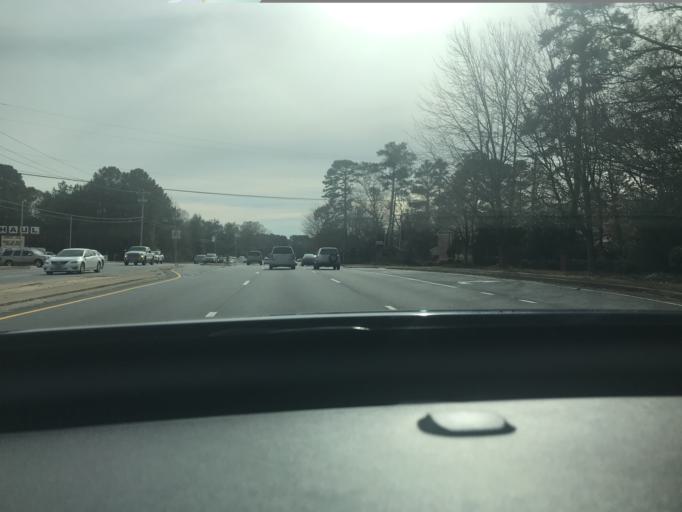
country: US
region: Georgia
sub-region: Gwinnett County
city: Lilburn
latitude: 33.9362
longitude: -84.1208
